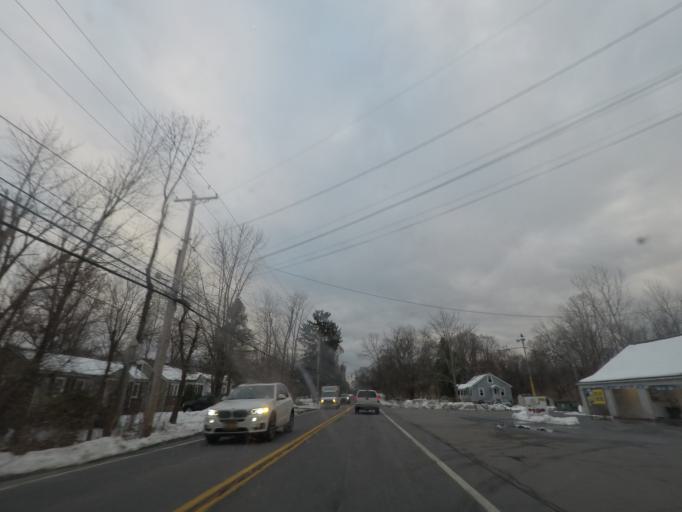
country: US
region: New York
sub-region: Ulster County
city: Plattekill
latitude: 41.5823
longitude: -74.0683
